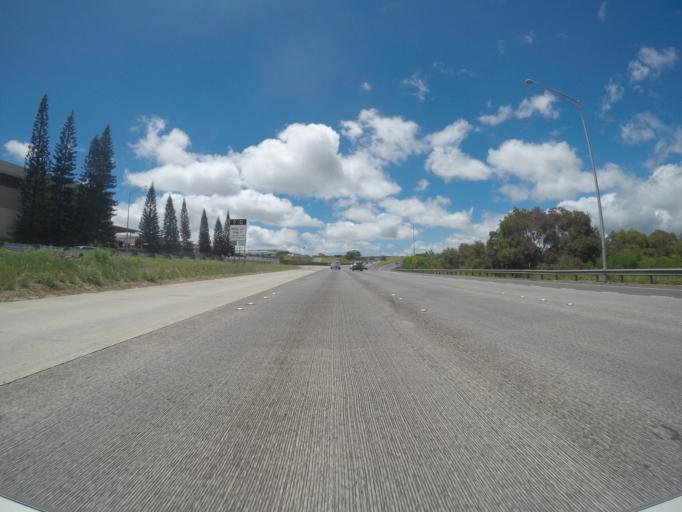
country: US
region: Hawaii
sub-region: Honolulu County
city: Waipio
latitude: 21.4244
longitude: -157.9953
